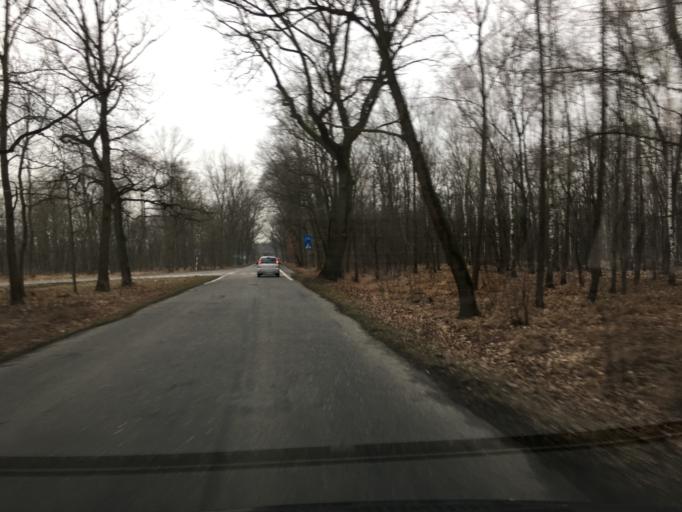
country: PL
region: Opole Voivodeship
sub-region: Powiat kedzierzynsko-kozielski
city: Kedzierzyn-Kozle
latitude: 50.3214
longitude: 18.2350
